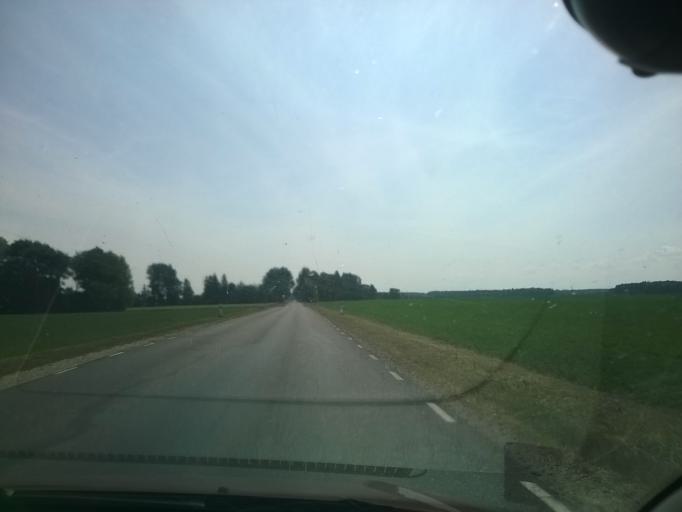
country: EE
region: Tartu
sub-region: Puhja vald
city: Puhja
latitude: 58.2749
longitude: 26.1757
